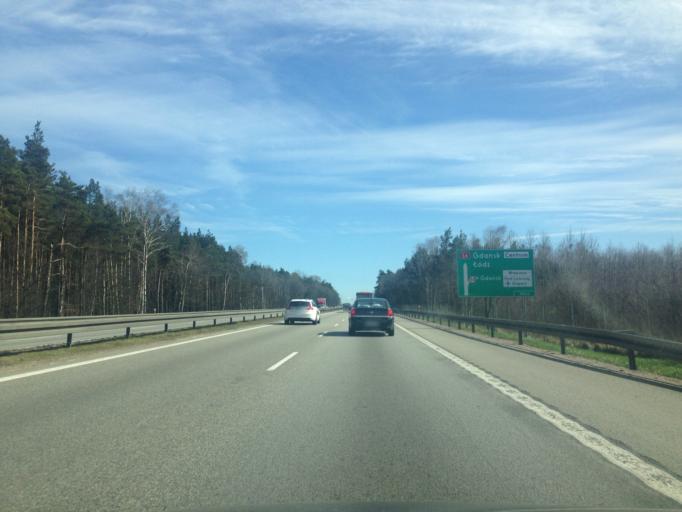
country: PL
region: Pomeranian Voivodeship
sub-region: Sopot
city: Sopot
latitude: 54.3862
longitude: 18.5005
